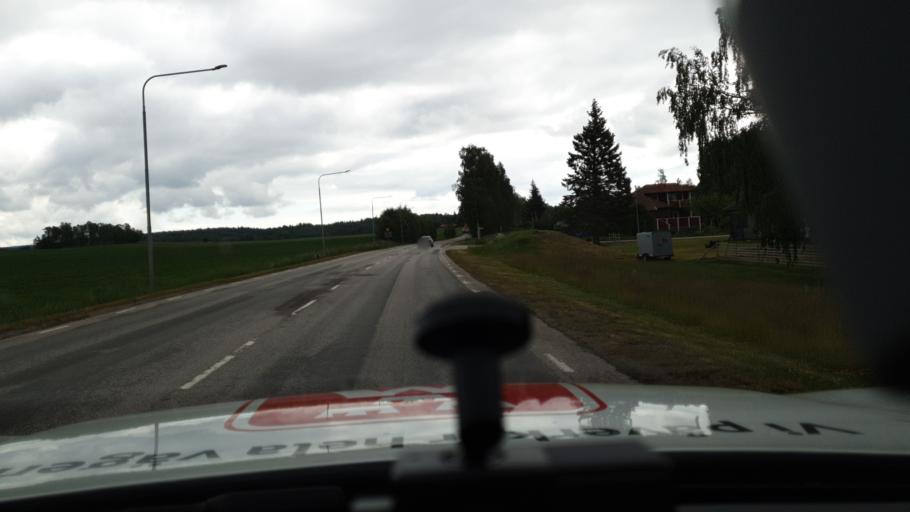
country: SE
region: Vaestra Goetaland
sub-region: Tibro Kommun
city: Tibro
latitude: 58.4159
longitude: 14.1896
